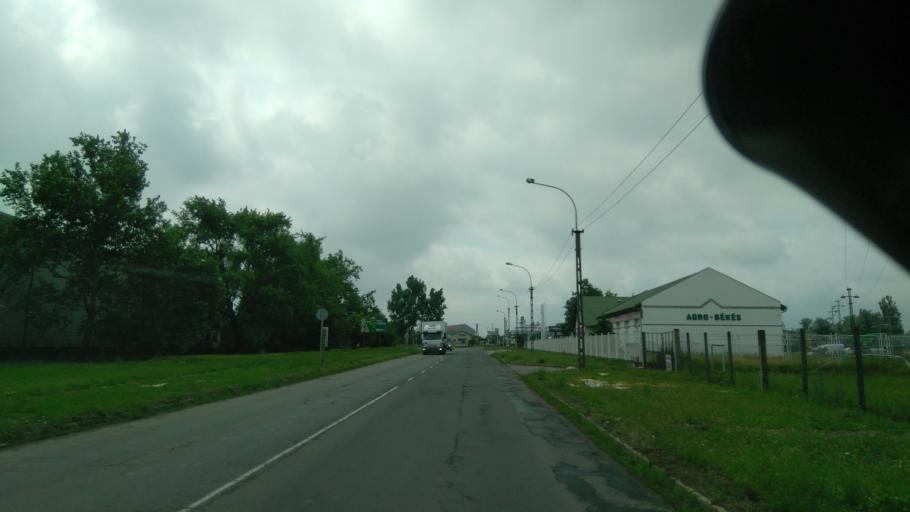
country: HU
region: Bekes
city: Bekescsaba
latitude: 46.6611
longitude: 21.0897
